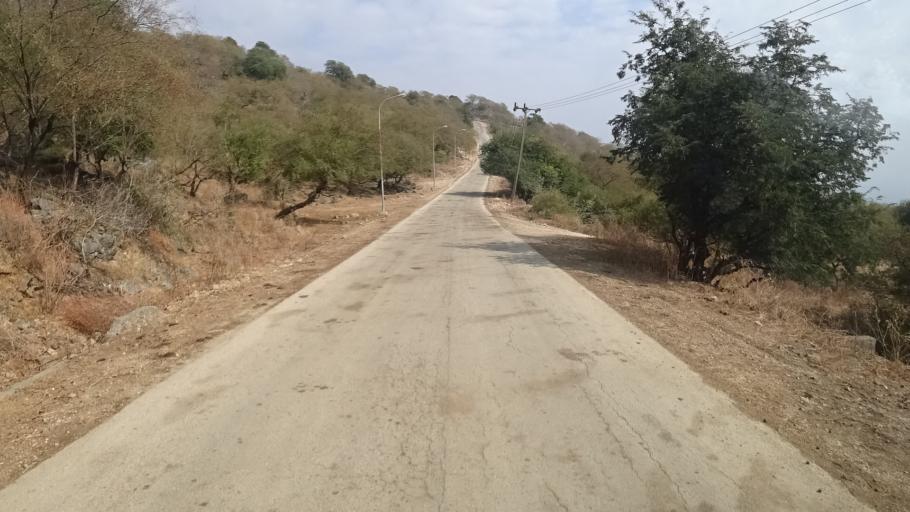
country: YE
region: Al Mahrah
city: Hawf
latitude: 16.7190
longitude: 53.2584
